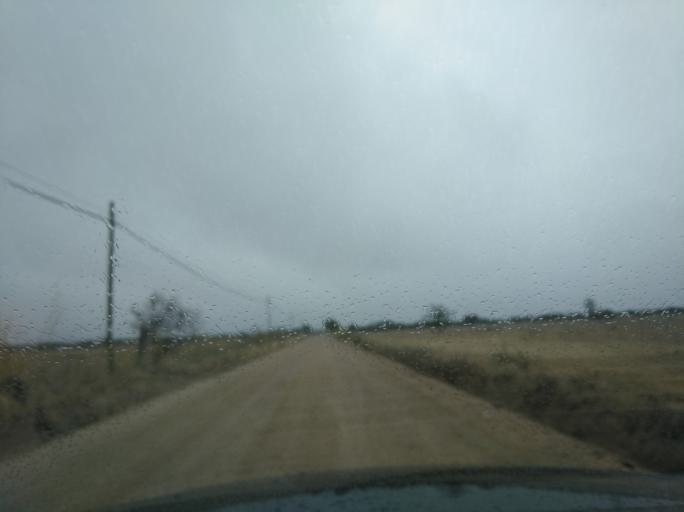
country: PT
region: Portalegre
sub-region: Campo Maior
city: Campo Maior
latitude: 38.9622
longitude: -7.0721
